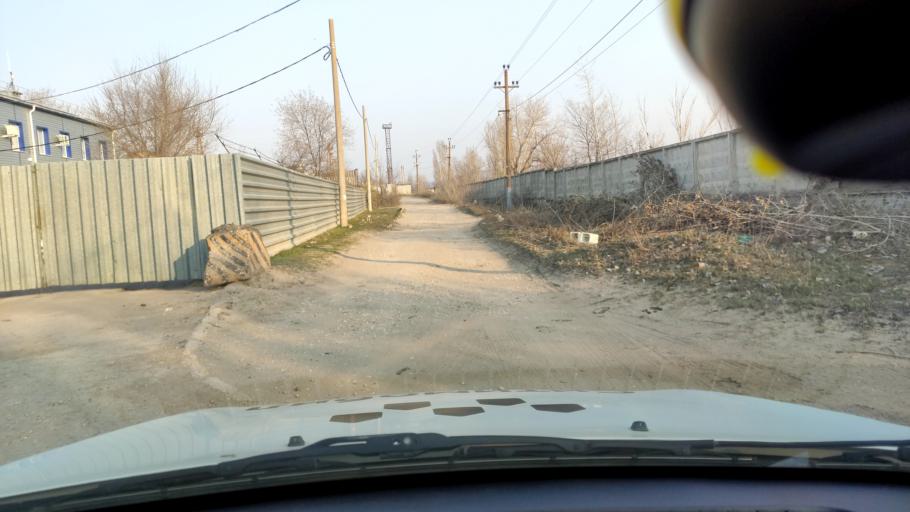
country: RU
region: Samara
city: Zhigulevsk
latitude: 53.4754
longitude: 49.5372
